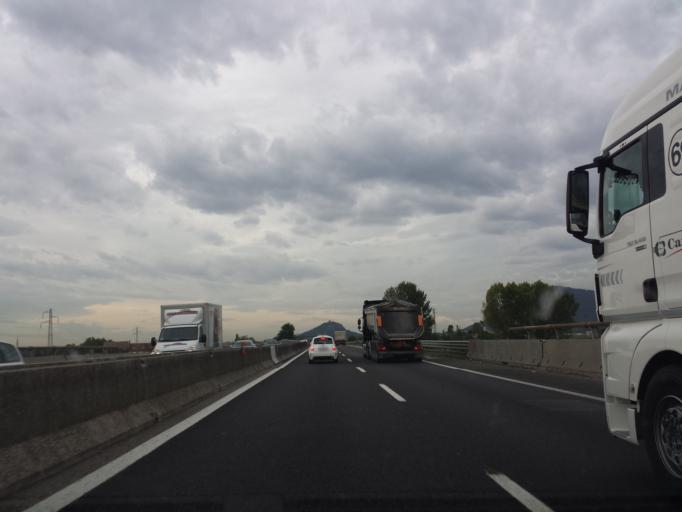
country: IT
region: Veneto
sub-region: Provincia di Padova
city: Battaglia Terme
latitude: 45.2805
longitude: 11.7921
